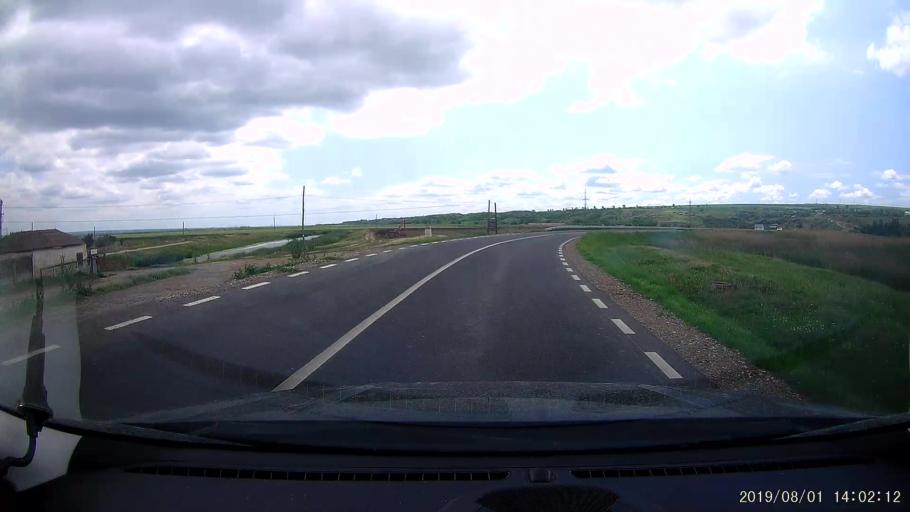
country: RO
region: Galati
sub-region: Comuna Foltesti
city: Foltesti
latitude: 45.7382
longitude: 28.0786
